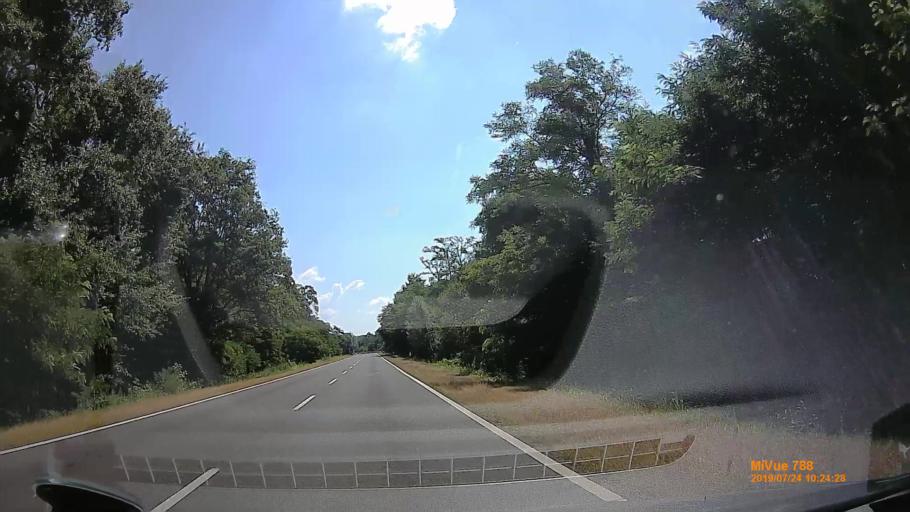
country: HU
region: Szabolcs-Szatmar-Bereg
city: Vasarosnameny
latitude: 48.1512
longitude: 22.3876
